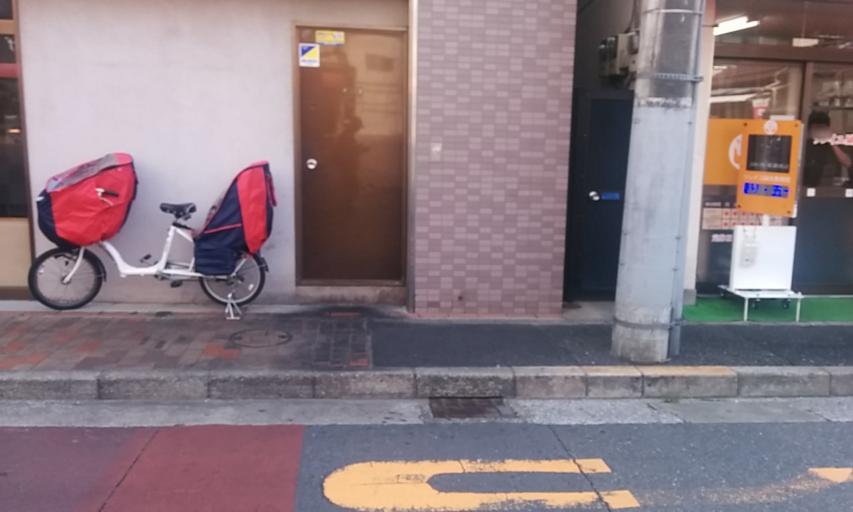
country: JP
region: Tokyo
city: Urayasu
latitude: 35.7048
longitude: 139.8451
